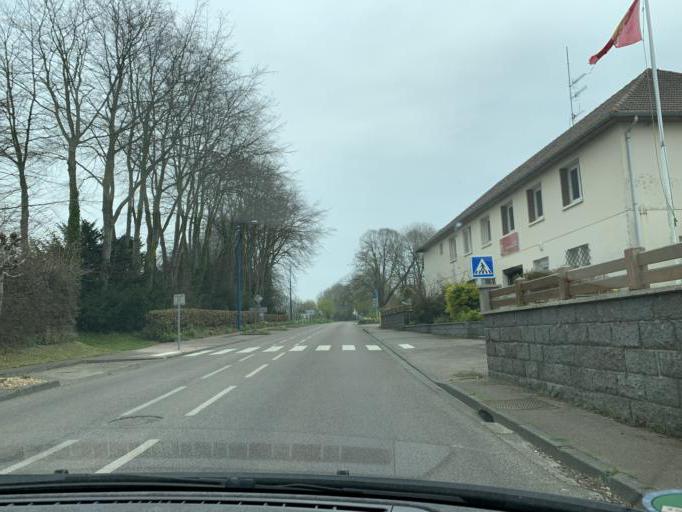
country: FR
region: Haute-Normandie
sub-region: Departement de la Seine-Maritime
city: Saint-Valery-en-Caux
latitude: 49.8585
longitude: 0.7208
